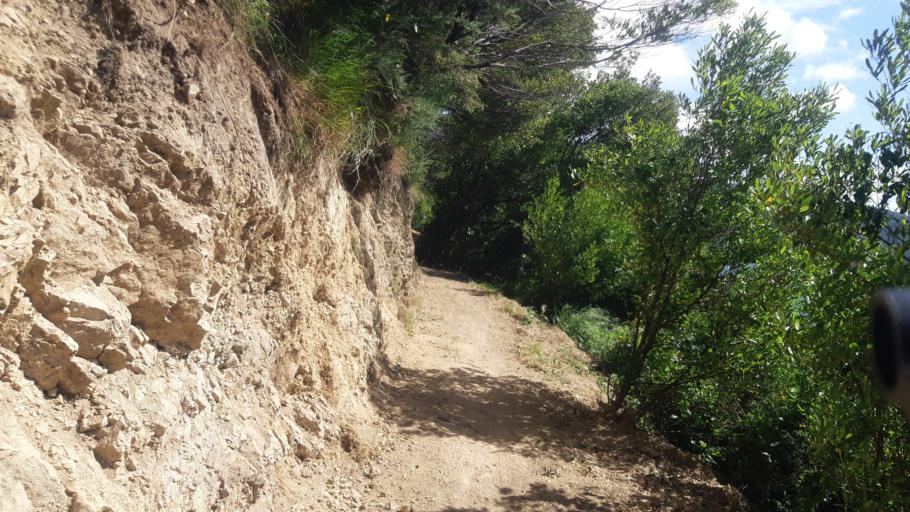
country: NZ
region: Marlborough
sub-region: Marlborough District
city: Picton
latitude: -41.2664
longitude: 174.0282
